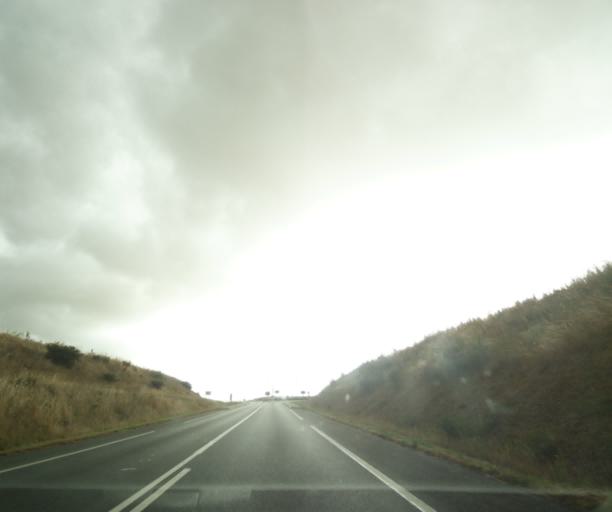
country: FR
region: Pays de la Loire
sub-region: Departement de la Vendee
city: Saint-Hilaire-de-Talmont
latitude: 46.4580
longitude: -1.6094
